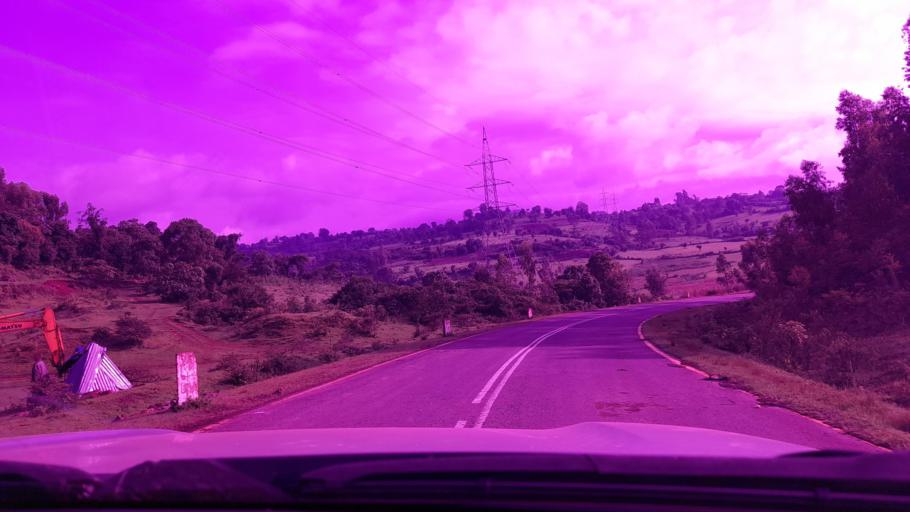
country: ET
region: Oromiya
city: Bedele
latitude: 8.2050
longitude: 36.4392
